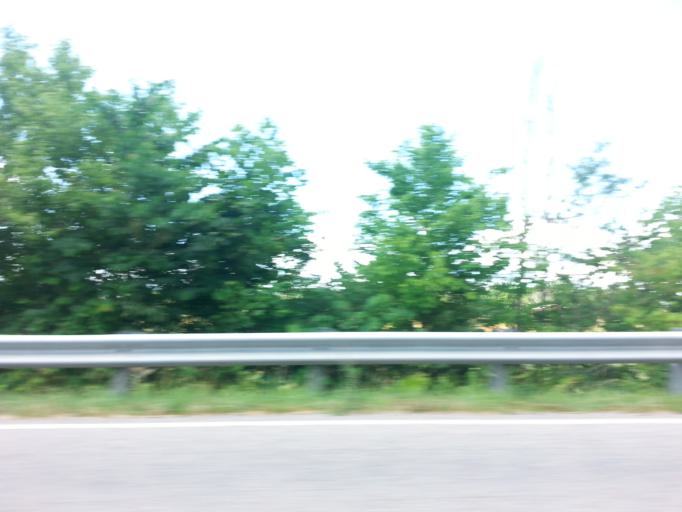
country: US
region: Virginia
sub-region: Lee County
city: Pennington Gap
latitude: 36.6972
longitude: -83.0452
